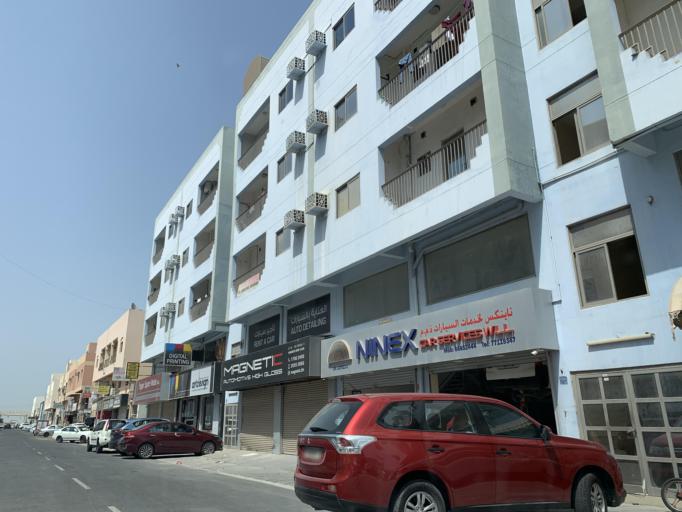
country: BH
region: Northern
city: Madinat `Isa
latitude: 26.1892
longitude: 50.5395
